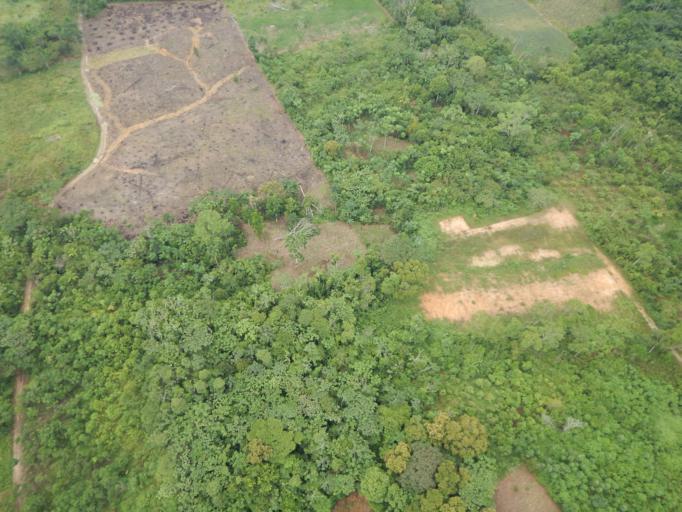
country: BO
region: Cochabamba
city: Chimore
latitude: -17.0923
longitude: -64.8408
